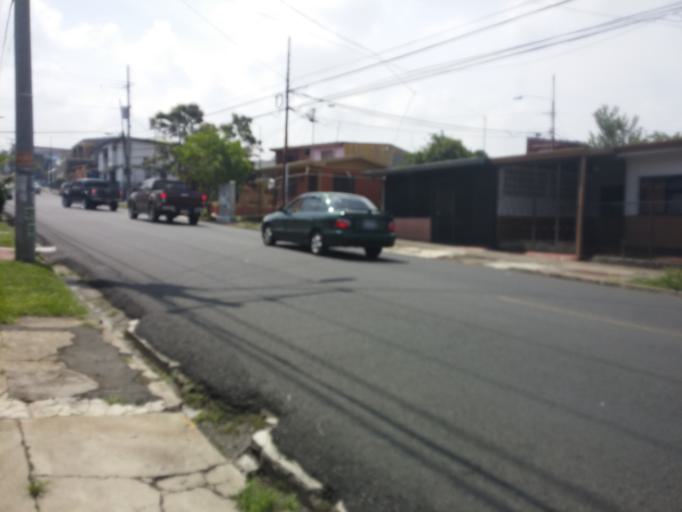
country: CR
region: Heredia
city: San Francisco
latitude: 9.9988
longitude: -84.1255
